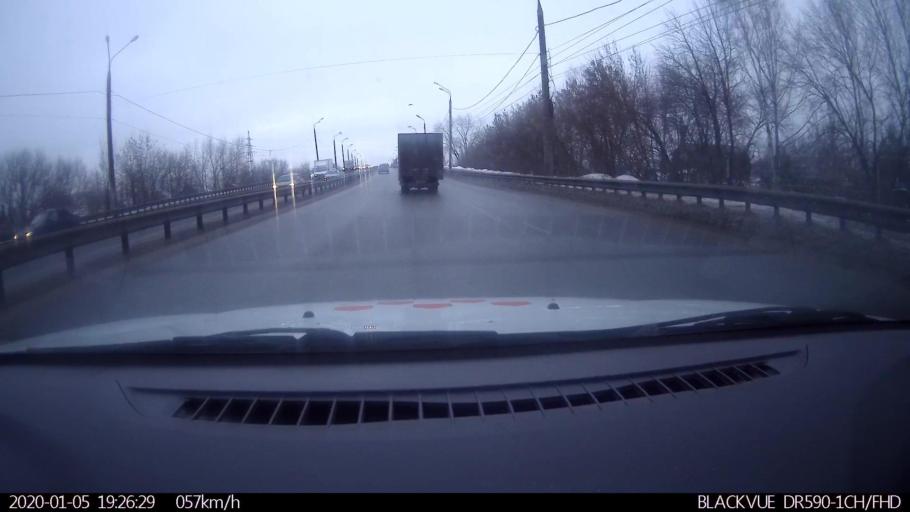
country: RU
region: Nizjnij Novgorod
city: Nizhniy Novgorod
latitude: 56.2986
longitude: 43.8780
